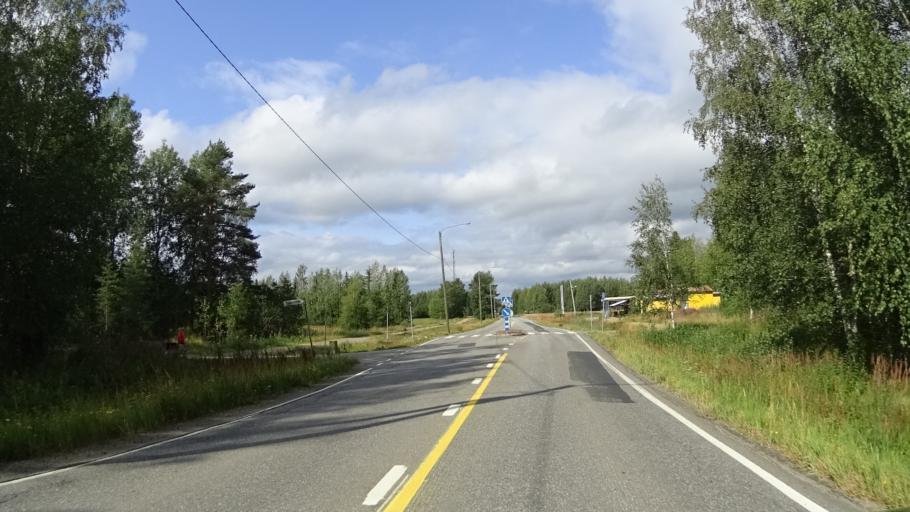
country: FI
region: Pirkanmaa
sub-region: Tampere
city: Luopioinen
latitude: 61.4828
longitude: 24.7116
